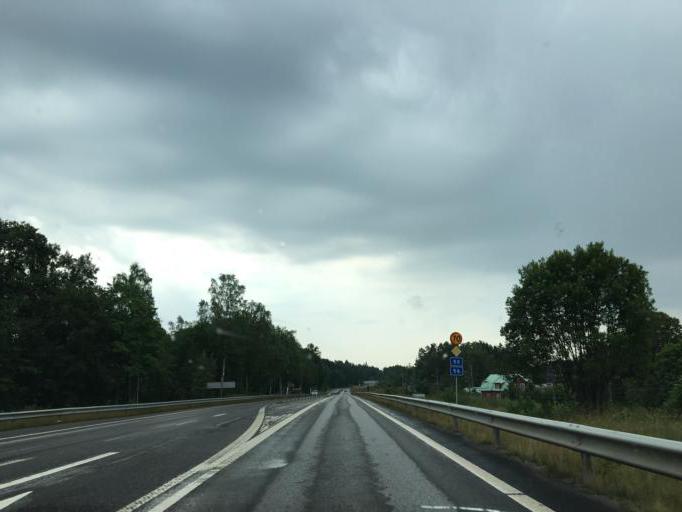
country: SE
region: OEstergoetland
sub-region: Norrkopings Kommun
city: Jursla
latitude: 58.7821
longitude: 16.1588
